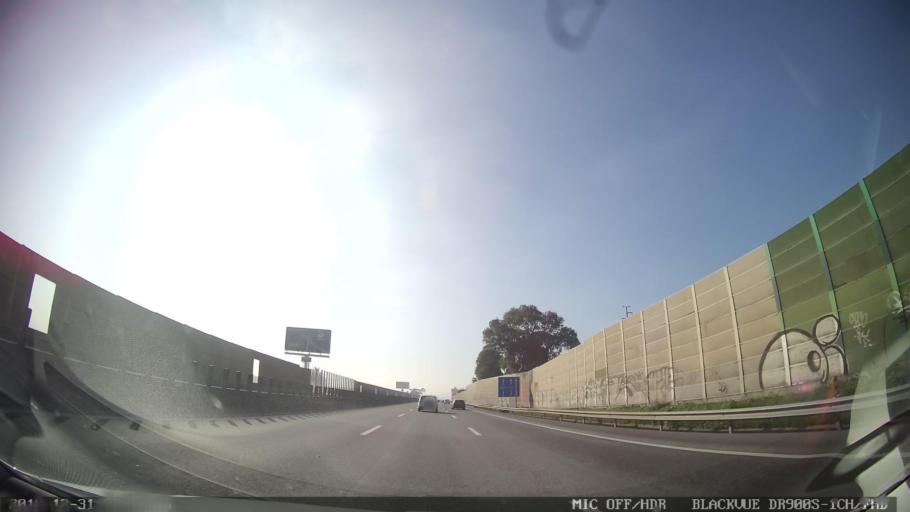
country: PT
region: Lisbon
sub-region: Vila Franca de Xira
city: Sobralinho
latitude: 38.9184
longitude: -9.0209
